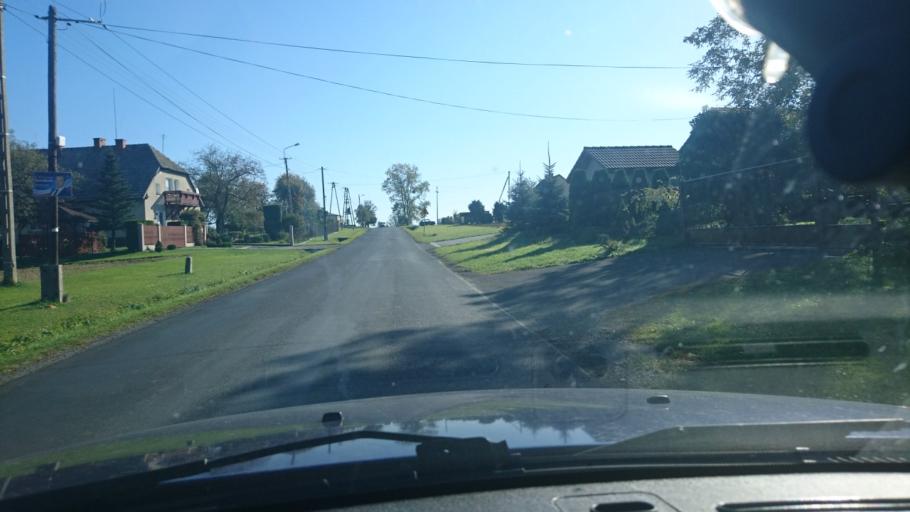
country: PL
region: Silesian Voivodeship
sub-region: Powiat bielski
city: Bronow
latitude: 49.8577
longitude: 18.9089
